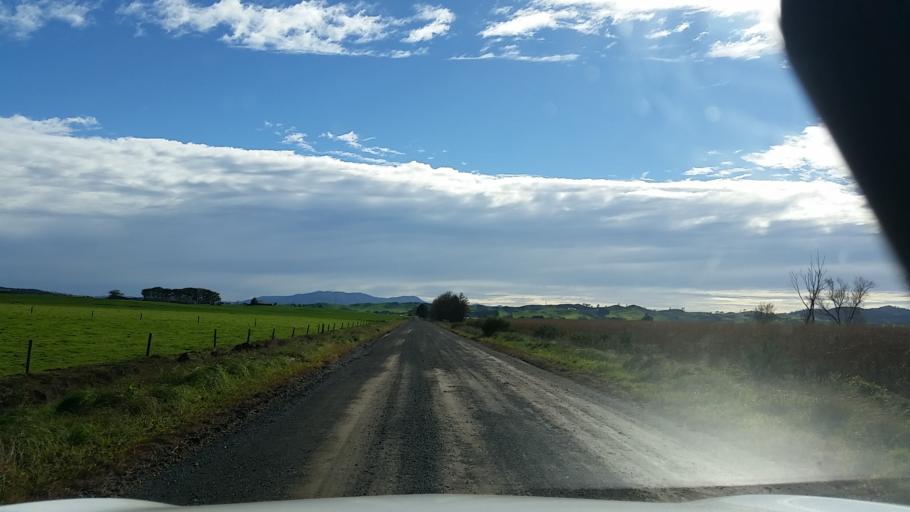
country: NZ
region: Waikato
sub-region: Hamilton City
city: Hamilton
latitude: -37.6313
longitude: 175.4284
